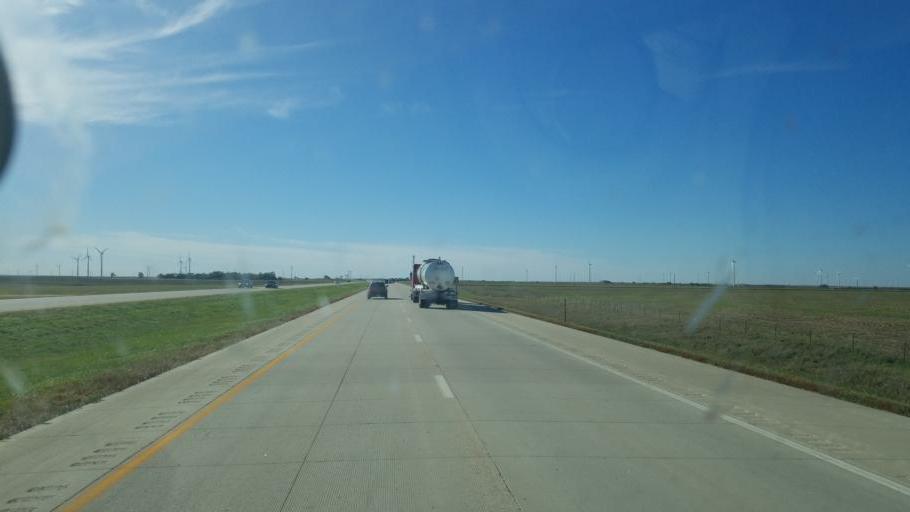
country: US
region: Kansas
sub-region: Ellsworth County
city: Ellsworth
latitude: 38.8495
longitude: -98.2575
